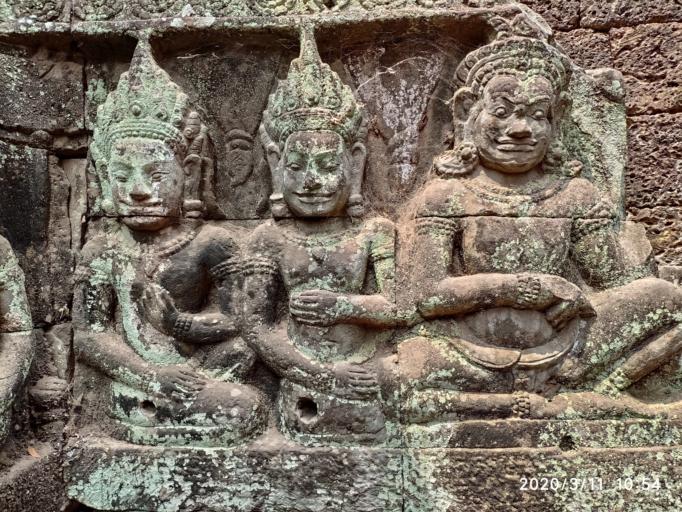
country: KH
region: Siem Reap
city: Siem Reap
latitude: 13.4477
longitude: 103.8589
